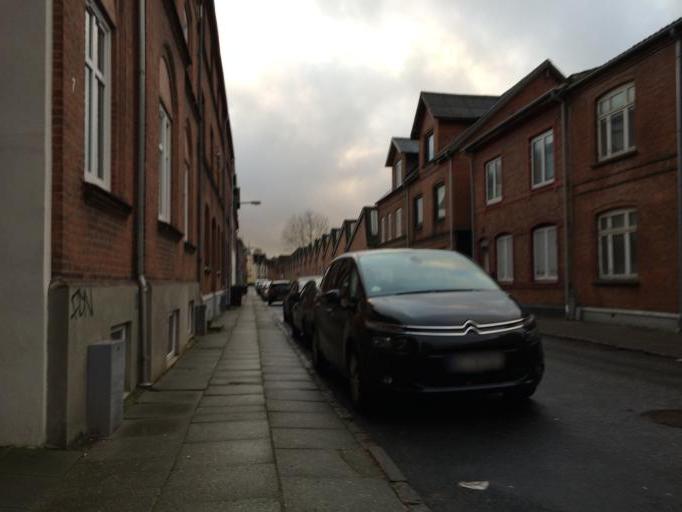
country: DK
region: South Denmark
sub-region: Vejle Kommune
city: Vejle
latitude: 55.7146
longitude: 9.5327
